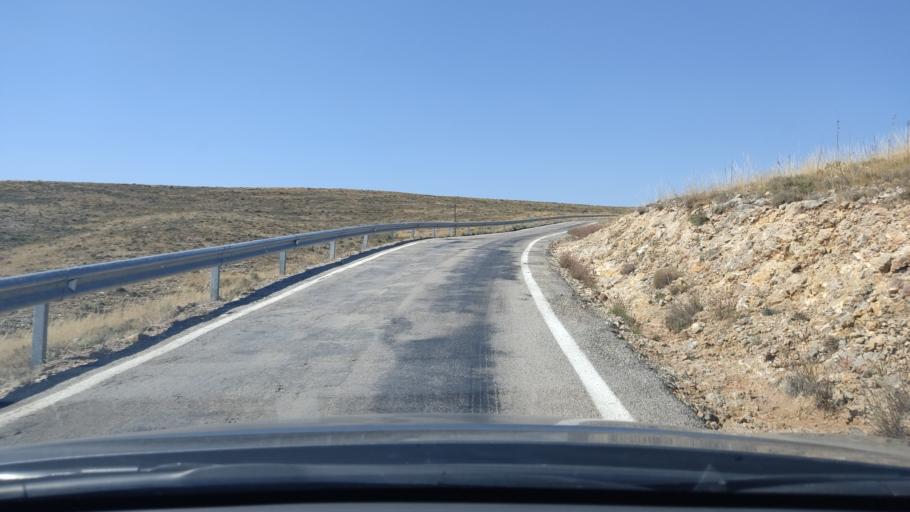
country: ES
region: Aragon
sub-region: Provincia de Teruel
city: Huesa del Comun
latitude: 41.0198
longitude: -0.9548
